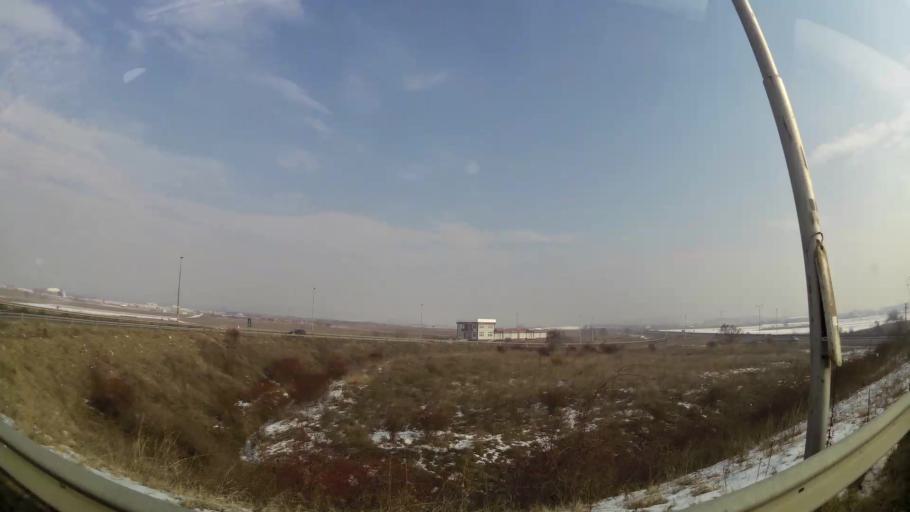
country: MK
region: Suto Orizari
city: Suto Orizare
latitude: 42.0537
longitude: 21.3813
